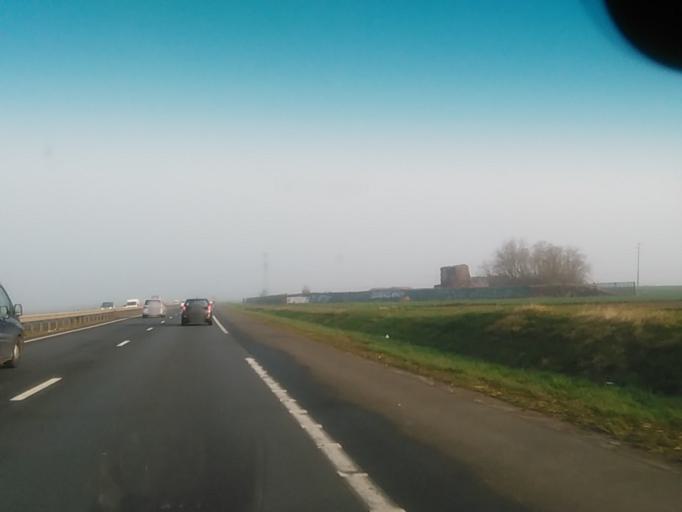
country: FR
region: Lower Normandy
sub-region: Departement du Calvados
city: Bourguebus
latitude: 49.0985
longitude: -0.3117
